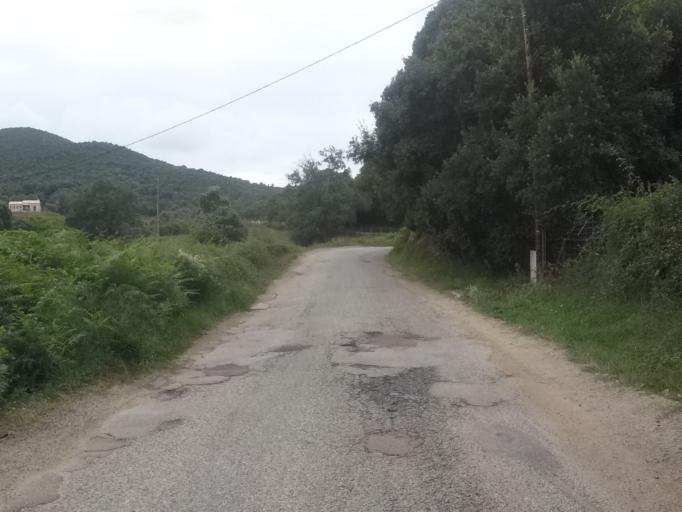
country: FR
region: Corsica
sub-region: Departement de la Corse-du-Sud
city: Pietrosella
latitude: 41.8133
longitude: 8.8506
